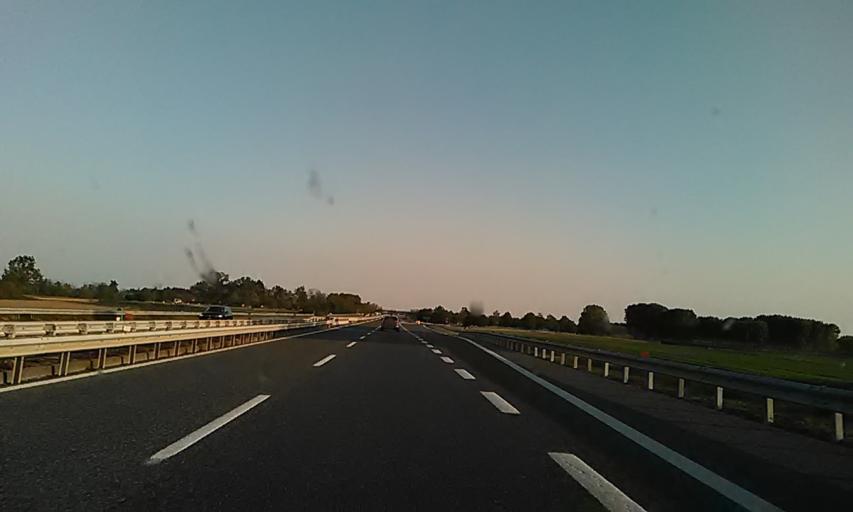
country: IT
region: Piedmont
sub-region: Provincia di Novara
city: Sillavengo
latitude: 45.5071
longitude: 8.4342
